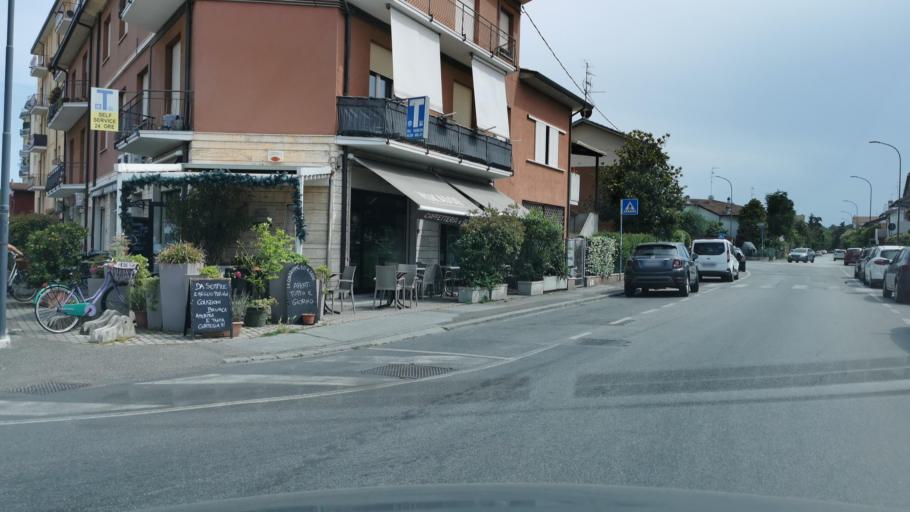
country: IT
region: Emilia-Romagna
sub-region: Provincia di Ravenna
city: Ravenna
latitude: 44.4180
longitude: 12.1821
